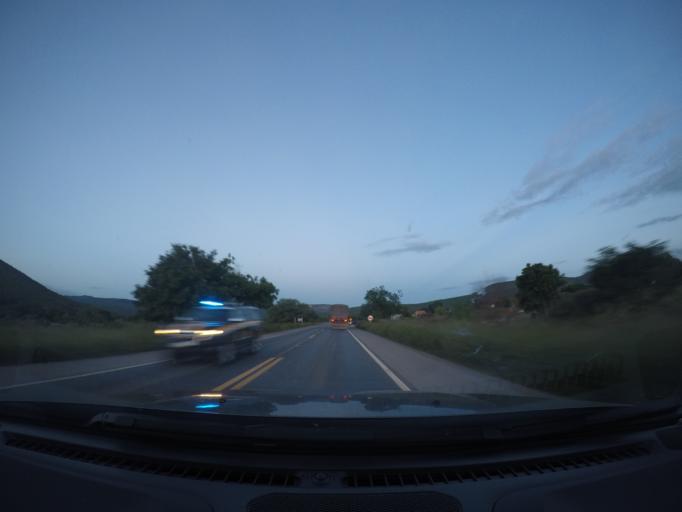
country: BR
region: Bahia
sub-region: Seabra
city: Seabra
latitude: -12.4863
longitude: -41.7256
